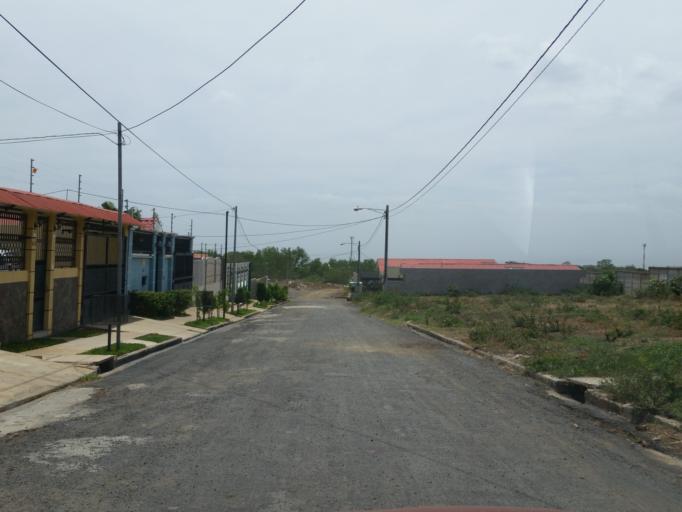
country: NI
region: Managua
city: Managua
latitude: 12.1110
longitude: -86.2421
